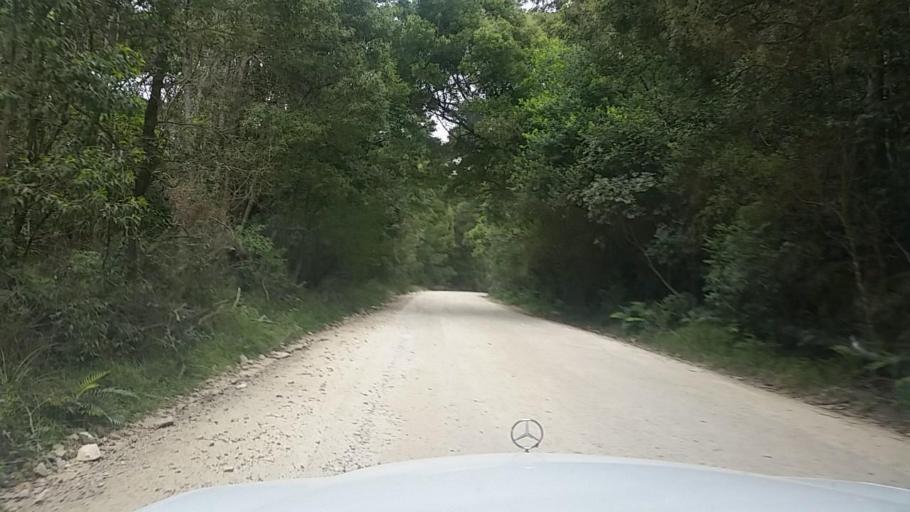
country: ZA
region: Western Cape
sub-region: Eden District Municipality
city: Knysna
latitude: -33.9754
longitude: 23.1431
